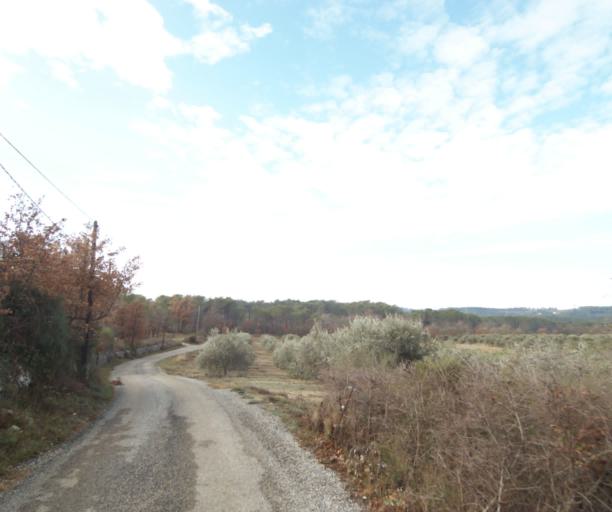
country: FR
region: Provence-Alpes-Cote d'Azur
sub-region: Departement du Var
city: Trans-en-Provence
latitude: 43.4967
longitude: 6.4617
